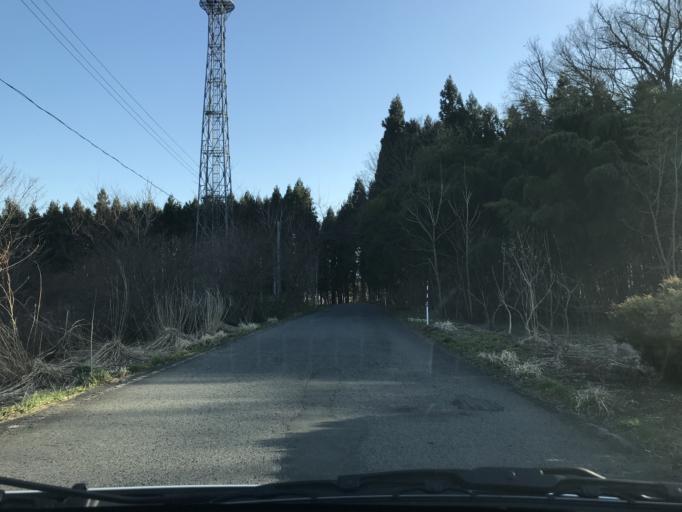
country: JP
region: Iwate
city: Kitakami
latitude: 39.2330
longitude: 141.0449
